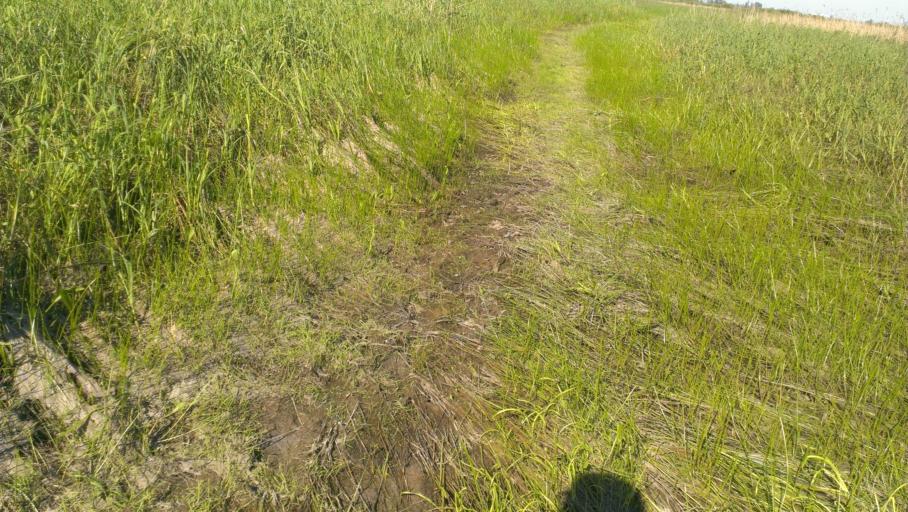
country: RU
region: Altai Krai
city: Novoaltaysk
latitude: 53.3640
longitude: 83.8606
